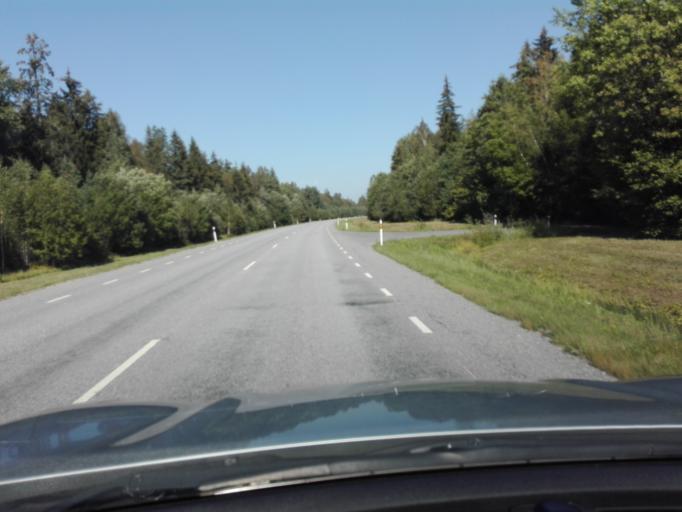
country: EE
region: Raplamaa
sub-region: Rapla vald
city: Rapla
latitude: 59.0070
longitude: 24.7695
